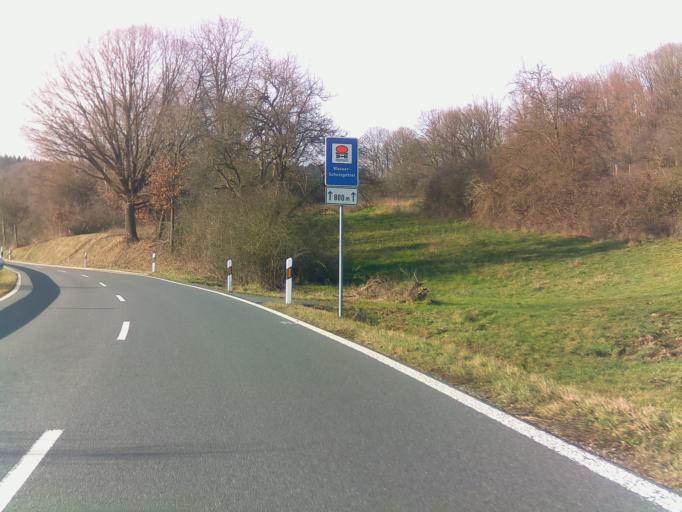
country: DE
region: Baden-Wuerttemberg
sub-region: Regierungsbezirk Stuttgart
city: Freudenberg
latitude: 49.7776
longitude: 9.3286
